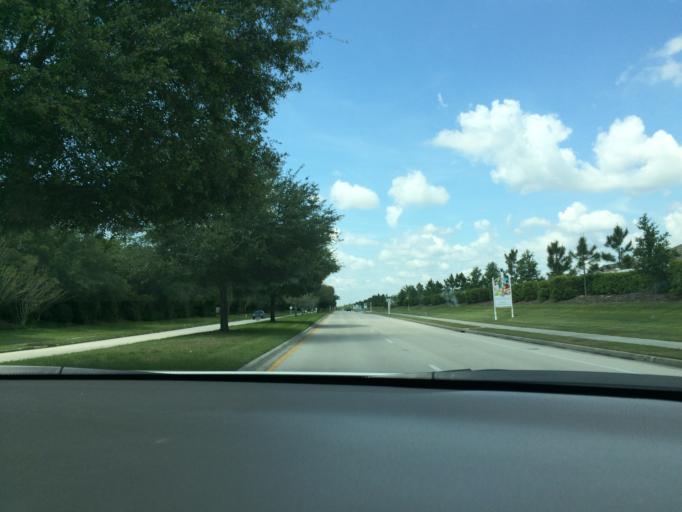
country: US
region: Florida
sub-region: Sarasota County
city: The Meadows
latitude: 27.4044
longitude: -82.3995
